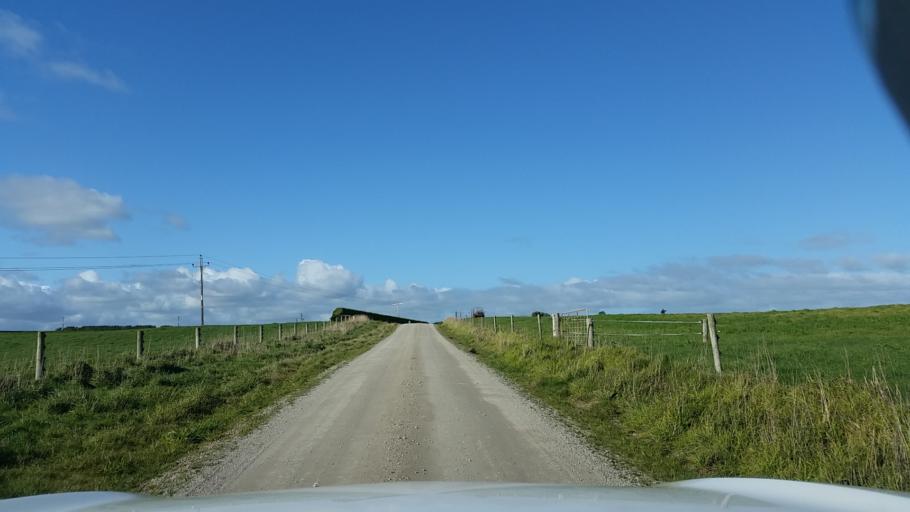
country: NZ
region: Taranaki
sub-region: South Taranaki District
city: Patea
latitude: -39.6852
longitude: 174.3936
